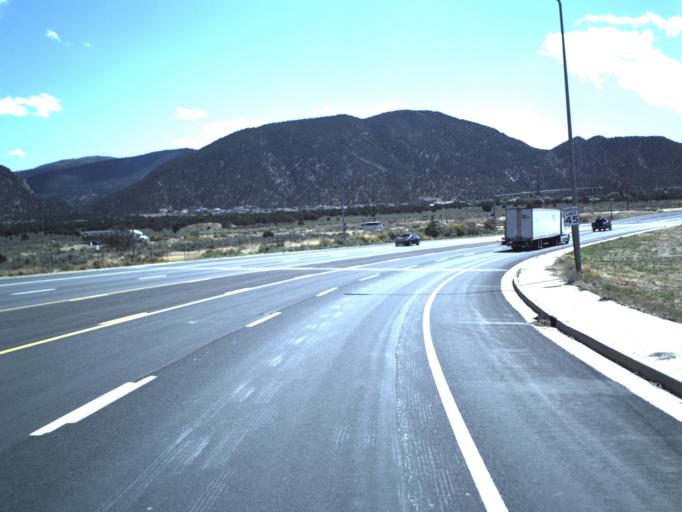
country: US
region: Utah
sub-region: Iron County
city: Cedar City
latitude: 37.7269
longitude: -113.0507
